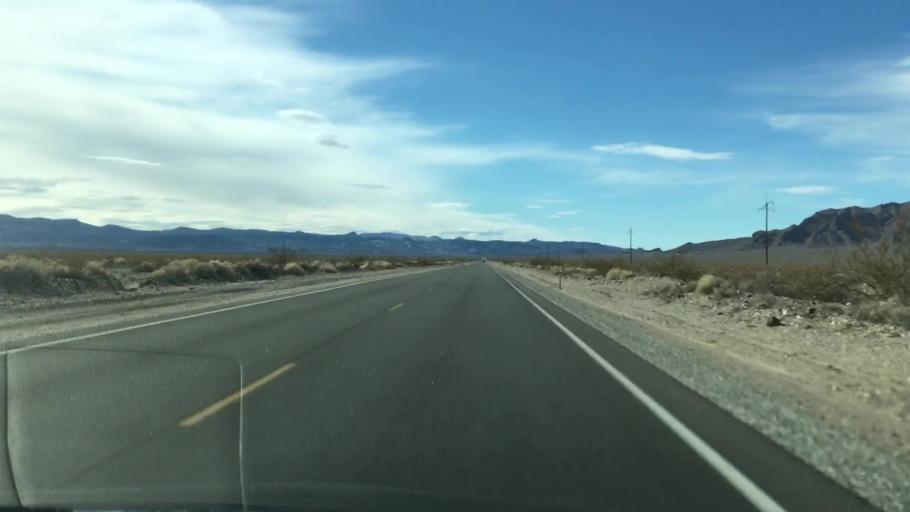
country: US
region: Nevada
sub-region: Nye County
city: Pahrump
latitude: 36.3042
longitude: -116.4385
